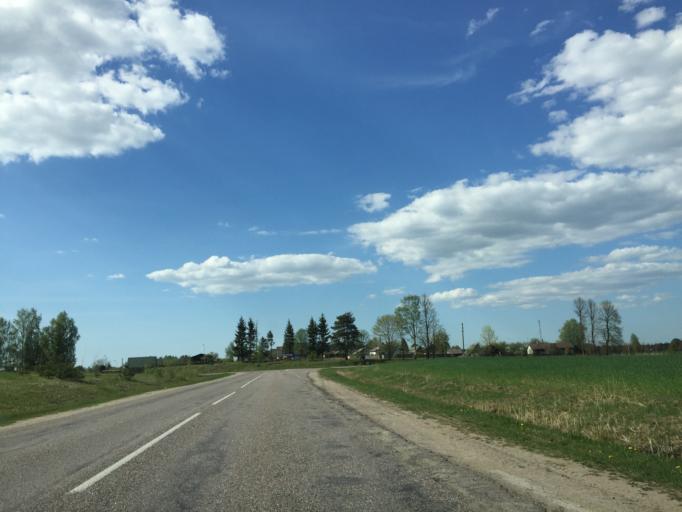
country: LV
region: Limbazu Rajons
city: Limbazi
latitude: 57.5126
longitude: 24.8146
